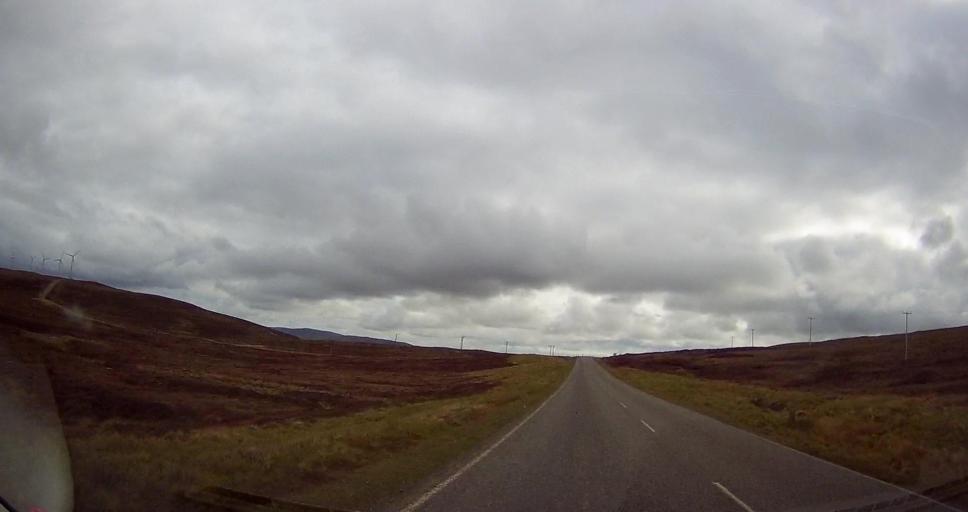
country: GB
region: Scotland
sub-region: Shetland Islands
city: Shetland
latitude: 60.6673
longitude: -1.0158
